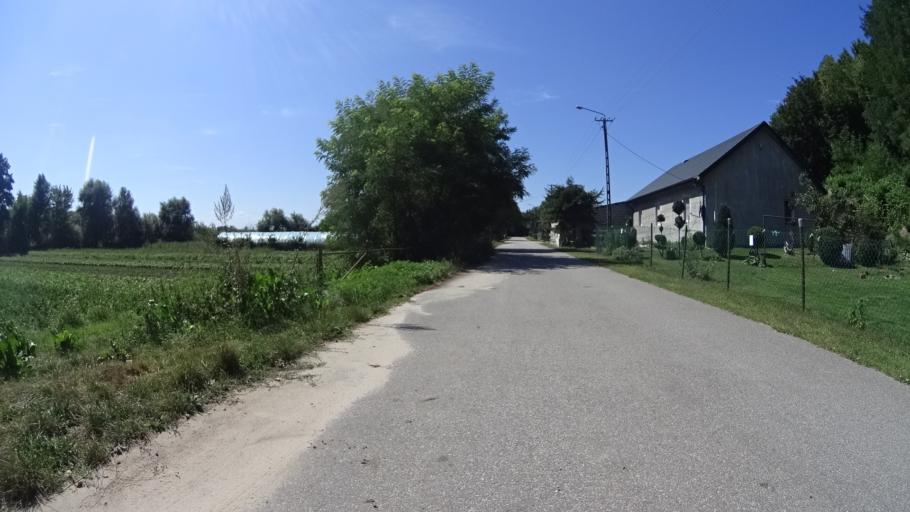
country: PL
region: Masovian Voivodeship
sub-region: Powiat bialobrzeski
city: Bialobrzegi
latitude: 51.6661
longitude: 20.8940
